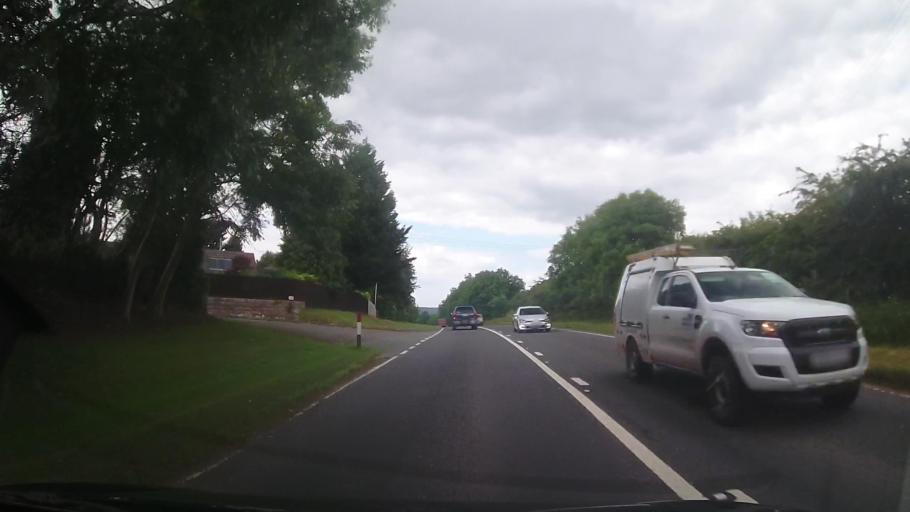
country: GB
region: England
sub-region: Herefordshire
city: Wellington
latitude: 52.0958
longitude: -2.7295
